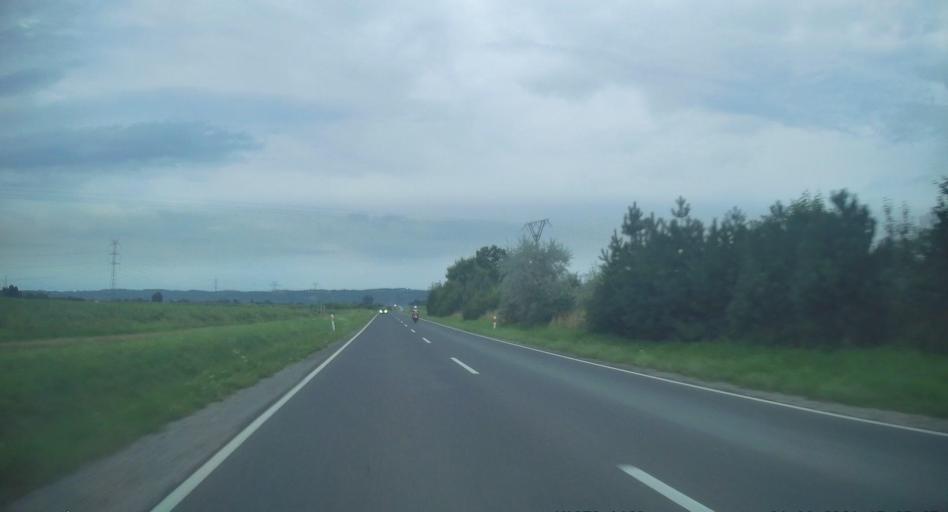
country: PL
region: Lesser Poland Voivodeship
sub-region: Powiat tarnowski
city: Wojnicz
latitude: 49.9710
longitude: 20.8453
